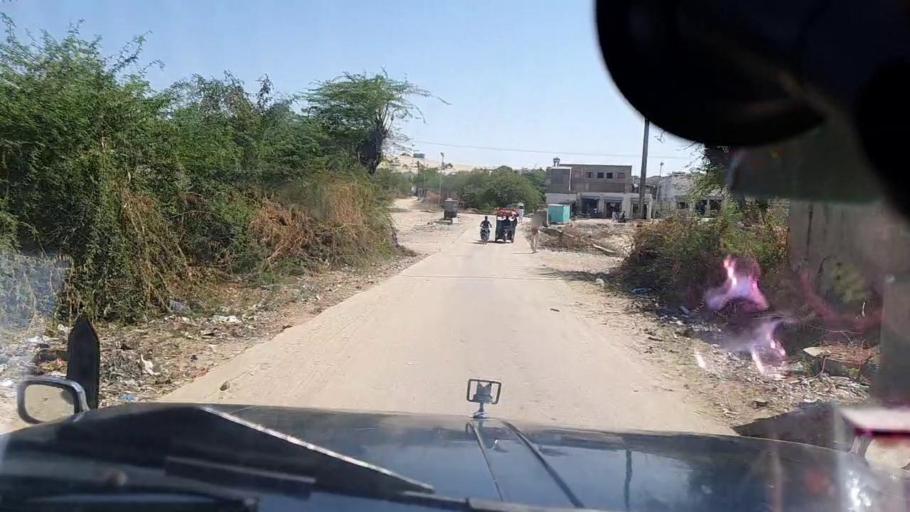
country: PK
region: Sindh
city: Diplo
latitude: 24.4644
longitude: 69.5848
